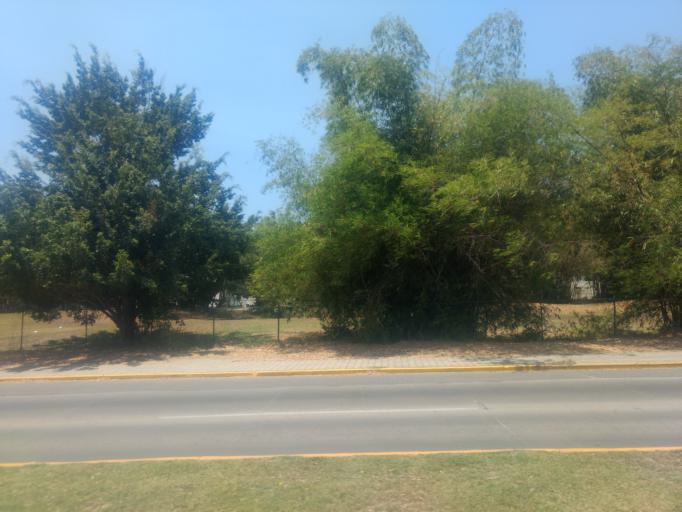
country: MX
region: Colima
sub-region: Manzanillo
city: Manzanillo
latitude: 19.1149
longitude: -104.3464
